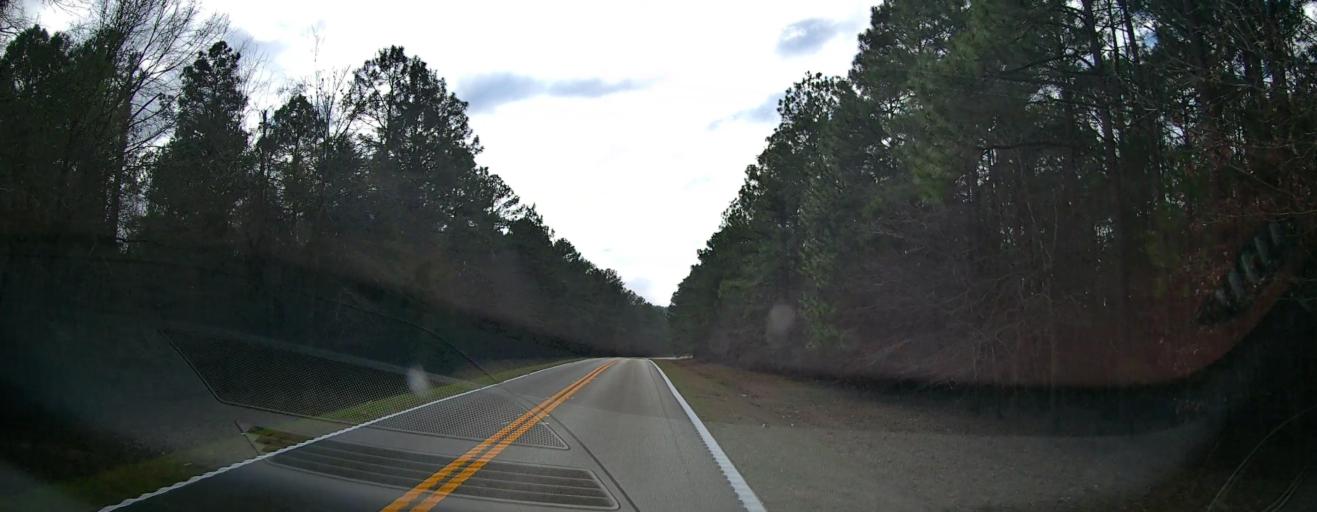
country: US
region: Georgia
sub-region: Marion County
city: Buena Vista
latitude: 32.4428
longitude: -84.4762
